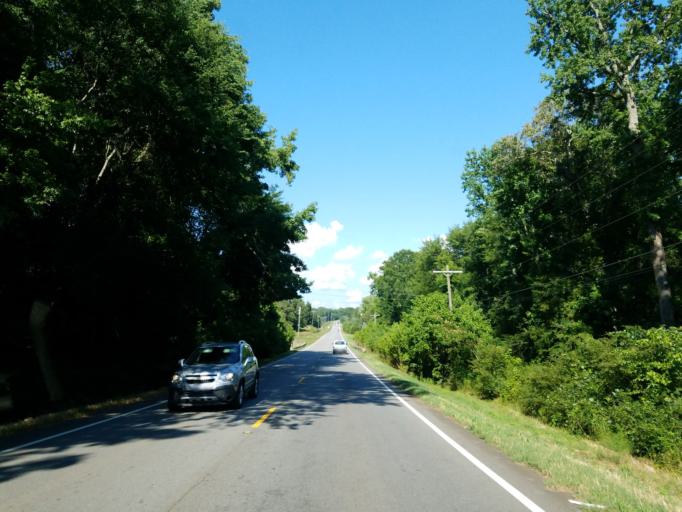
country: US
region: Georgia
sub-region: Peach County
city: Fort Valley
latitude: 32.5544
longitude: -83.8624
